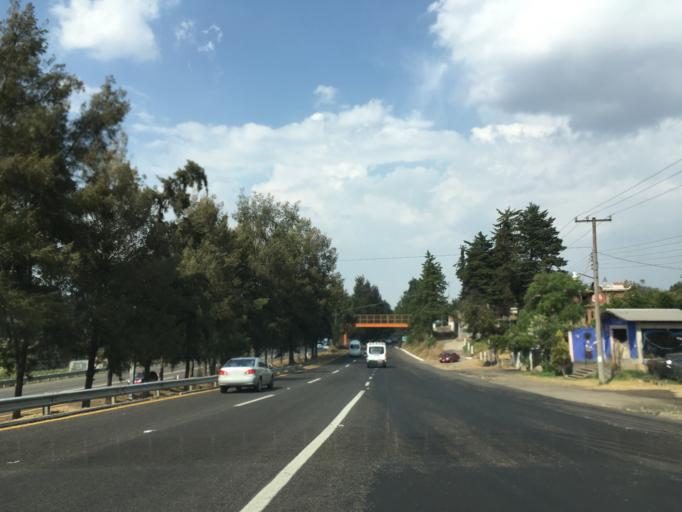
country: MX
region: Michoacan
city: Patzcuaro
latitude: 19.5305
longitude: -101.5600
